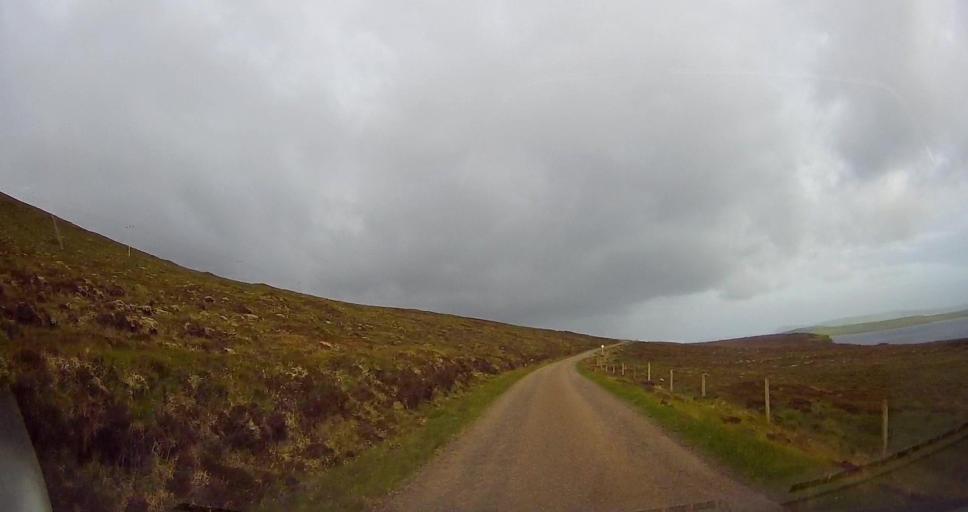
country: GB
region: Scotland
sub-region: Orkney Islands
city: Stromness
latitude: 58.8912
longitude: -3.2601
